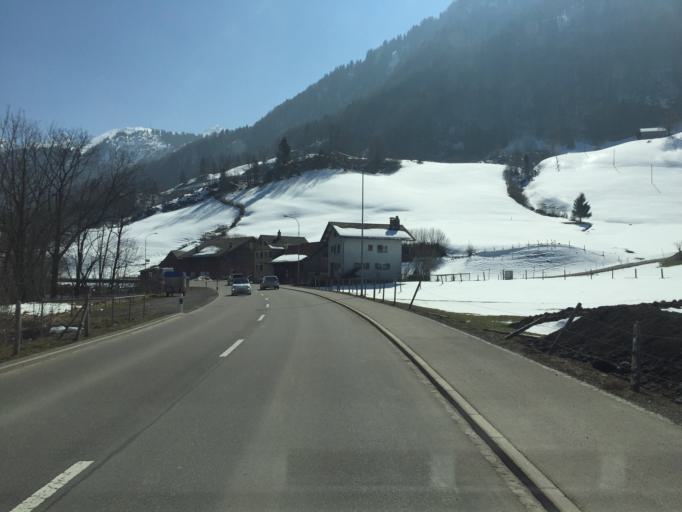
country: CH
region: Saint Gallen
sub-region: Wahlkreis Toggenburg
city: Krummenau
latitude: 47.1942
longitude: 9.2296
